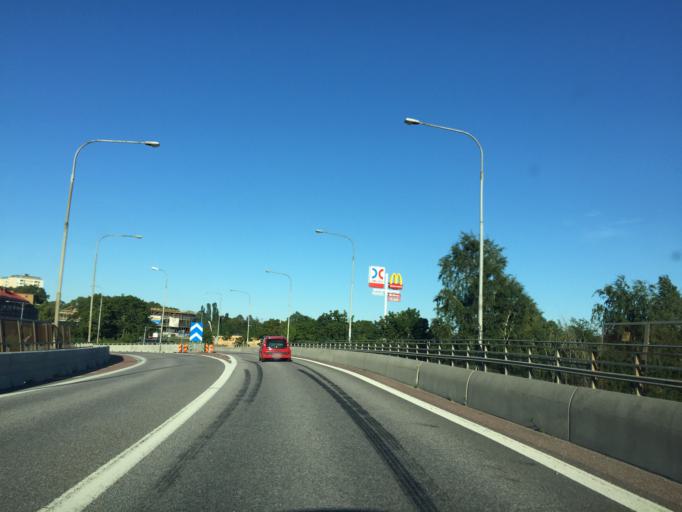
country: SE
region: OErebro
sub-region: Orebro Kommun
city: Orebro
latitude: 59.2648
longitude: 15.1959
